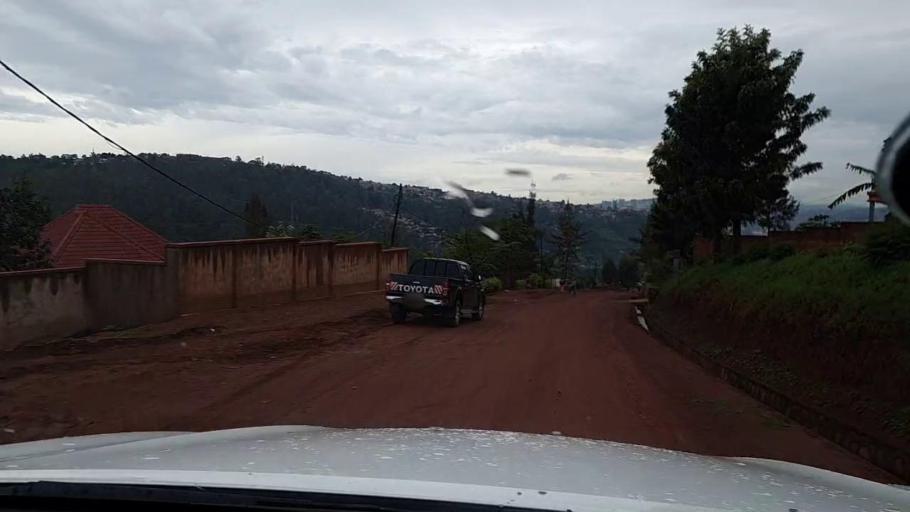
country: RW
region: Kigali
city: Kigali
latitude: -1.9052
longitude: 30.0458
